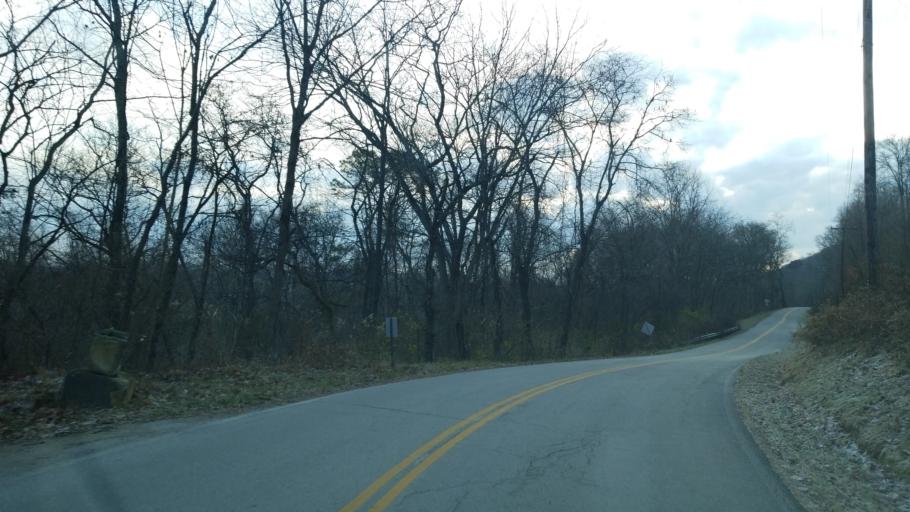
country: US
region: Ohio
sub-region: Ross County
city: Chillicothe
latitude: 39.2347
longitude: -82.8929
